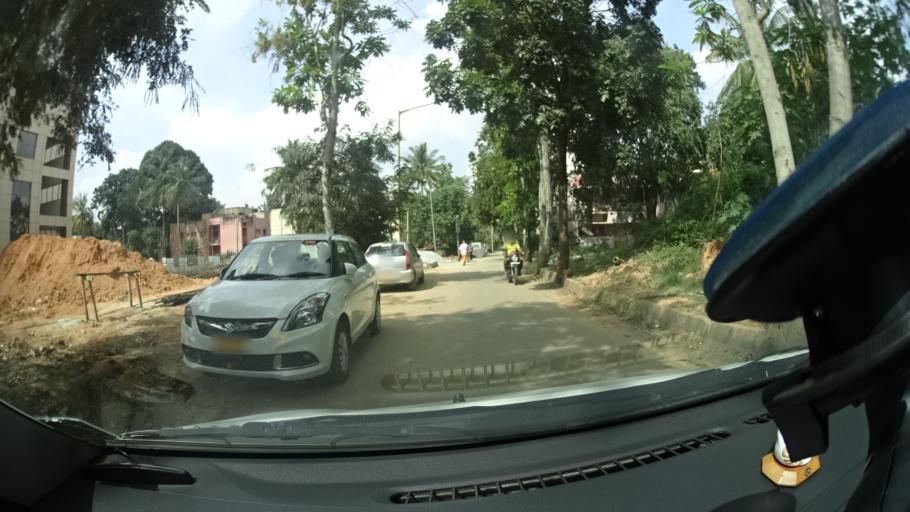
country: IN
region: Karnataka
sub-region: Bangalore Urban
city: Yelahanka
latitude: 13.0980
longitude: 77.5842
